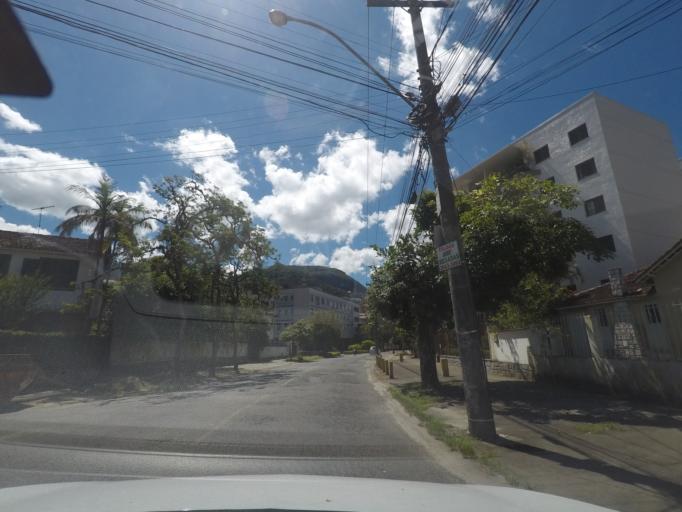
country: BR
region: Rio de Janeiro
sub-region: Teresopolis
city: Teresopolis
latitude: -22.4339
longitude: -42.9763
